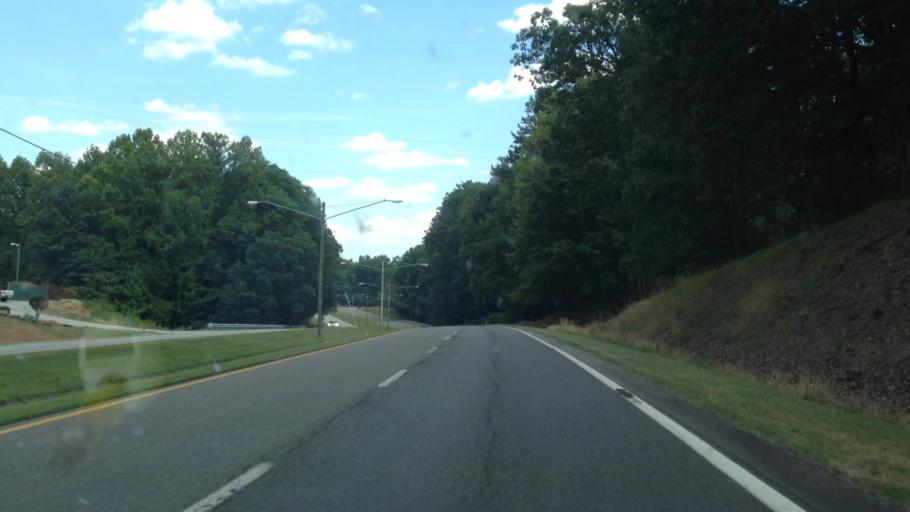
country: US
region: Virginia
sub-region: City of Danville
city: Danville
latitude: 36.5959
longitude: -79.5040
